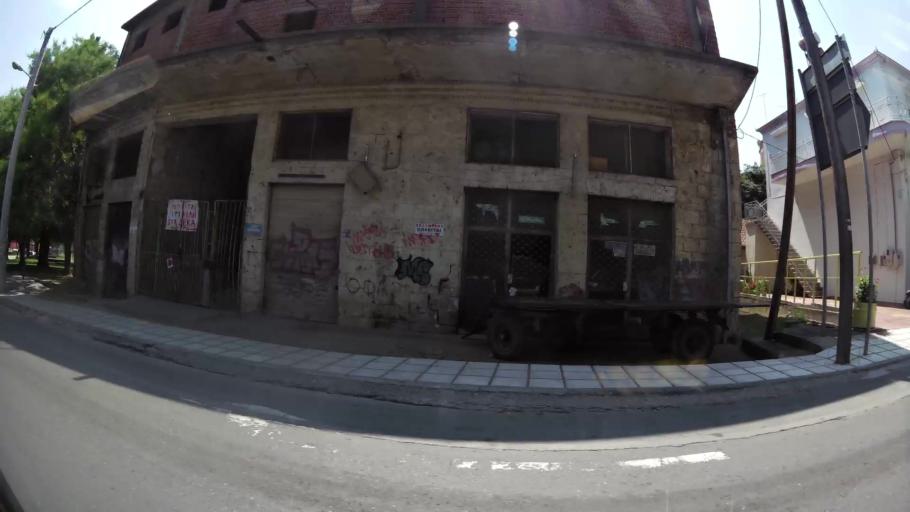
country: GR
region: Central Macedonia
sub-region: Nomos Imathias
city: Veroia
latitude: 40.5309
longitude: 22.2007
